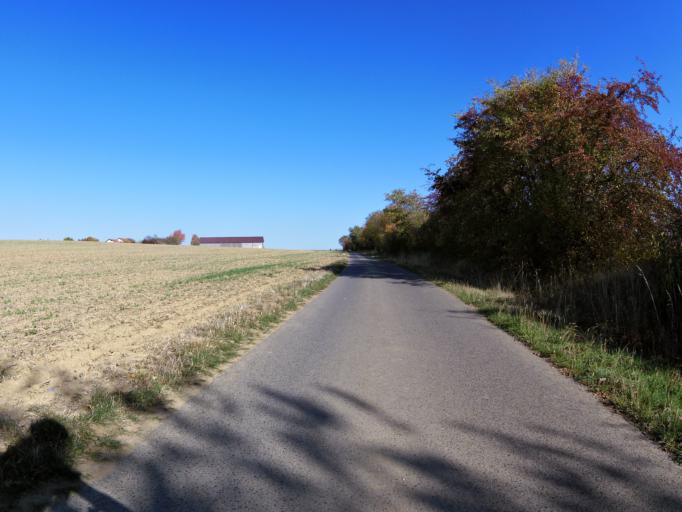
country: DE
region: Bavaria
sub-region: Regierungsbezirk Unterfranken
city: Eibelstadt
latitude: 49.7142
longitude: 9.9672
